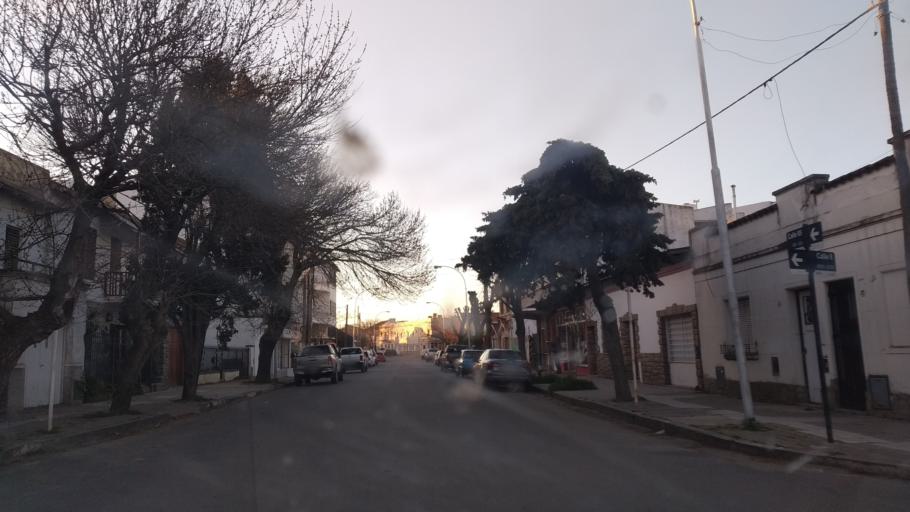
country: AR
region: Buenos Aires
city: Necochea
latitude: -38.5802
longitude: -58.7321
